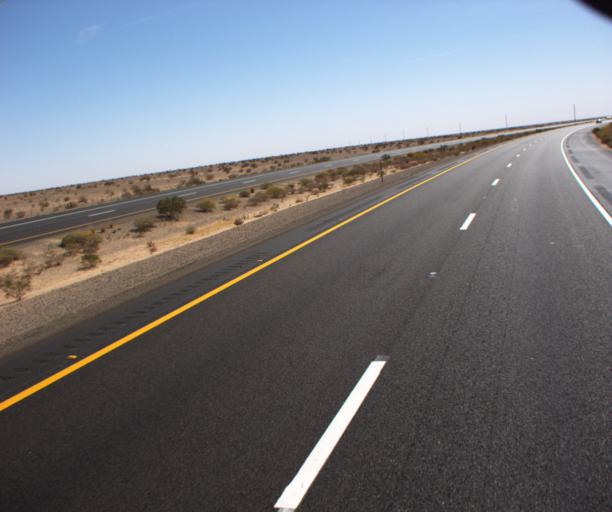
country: US
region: Arizona
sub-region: Yuma County
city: Somerton
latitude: 32.5013
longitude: -114.5595
